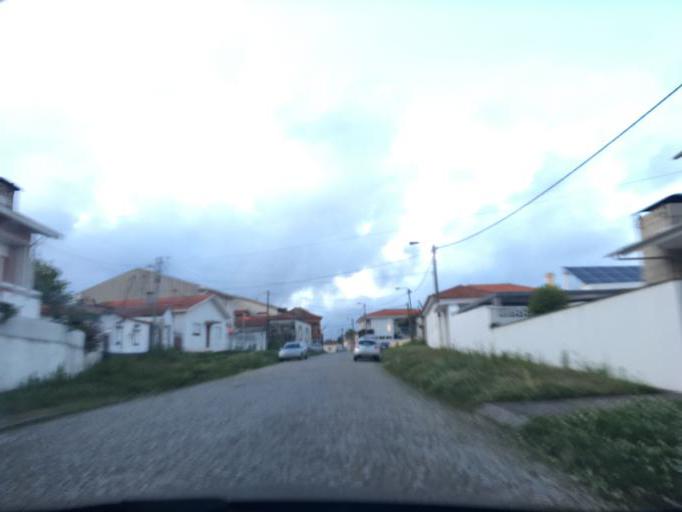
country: PT
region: Porto
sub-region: Maia
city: Anta
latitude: 41.2480
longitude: -8.6362
